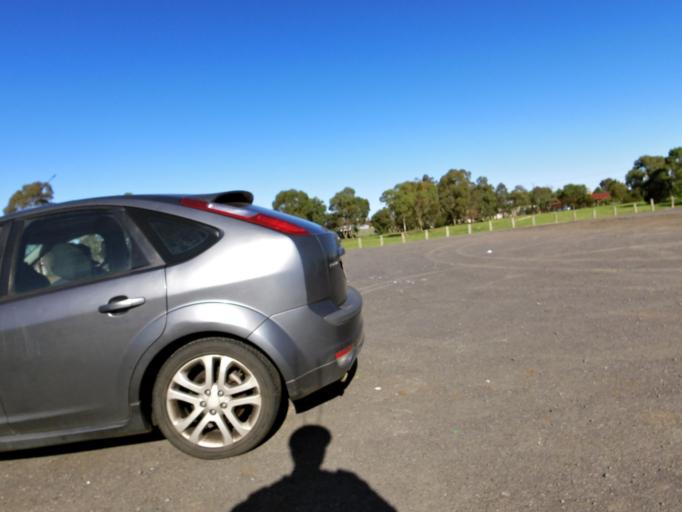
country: AU
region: Victoria
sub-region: Wyndham
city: Werribee
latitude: -37.8849
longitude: 144.6691
